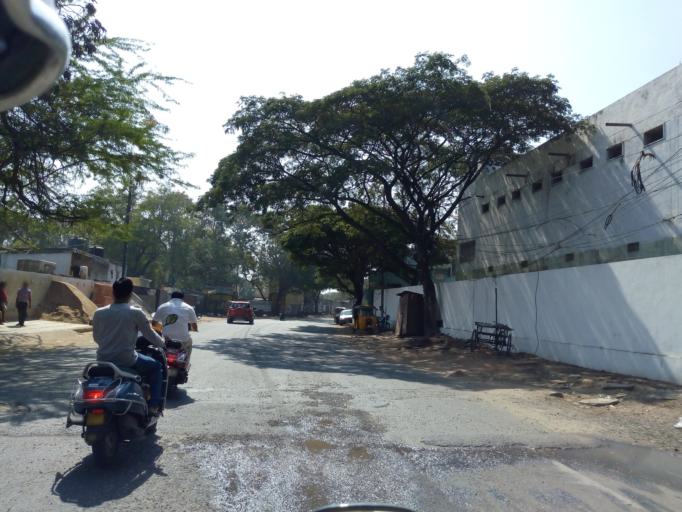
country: IN
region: Telangana
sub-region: Hyderabad
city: Malkajgiri
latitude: 17.4289
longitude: 78.4922
